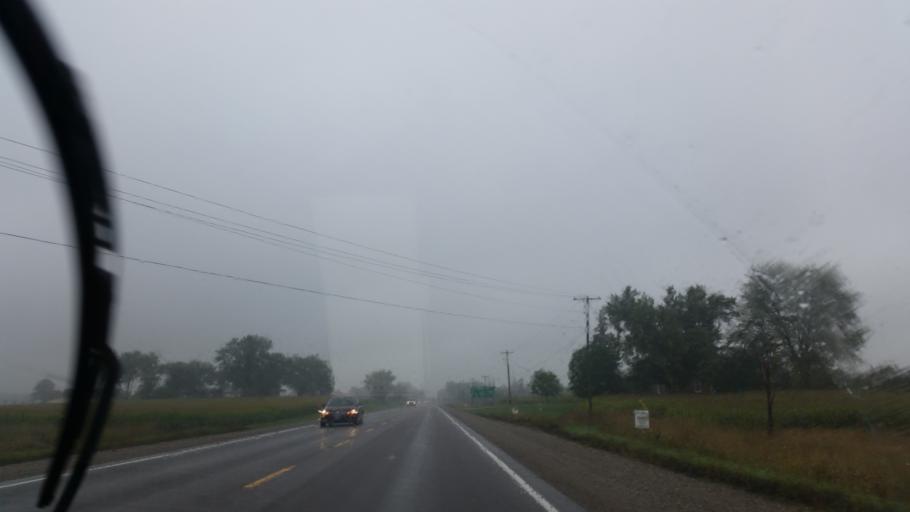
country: CA
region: Ontario
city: Stratford
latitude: 43.3131
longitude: -81.0319
